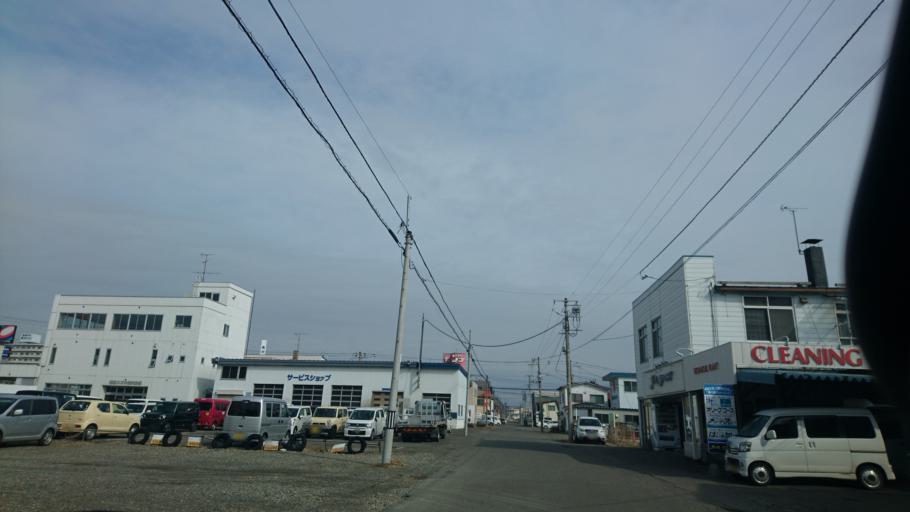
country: JP
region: Hokkaido
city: Obihiro
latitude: 42.9266
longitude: 143.2056
